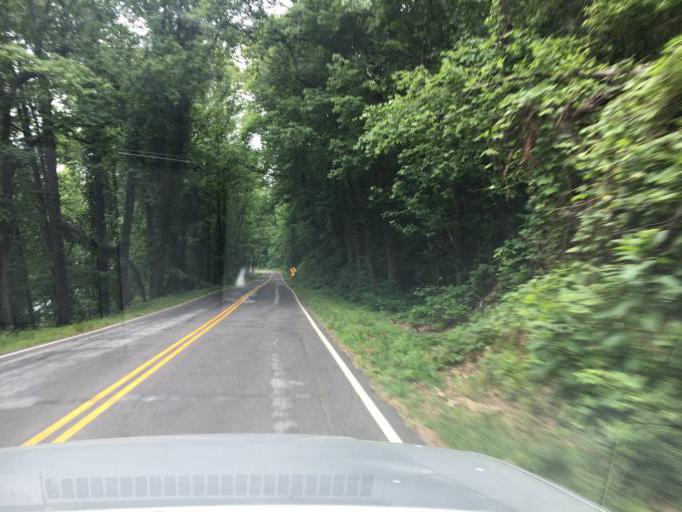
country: US
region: South Carolina
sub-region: Greenville County
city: Tigerville
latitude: 35.1571
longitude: -82.4158
